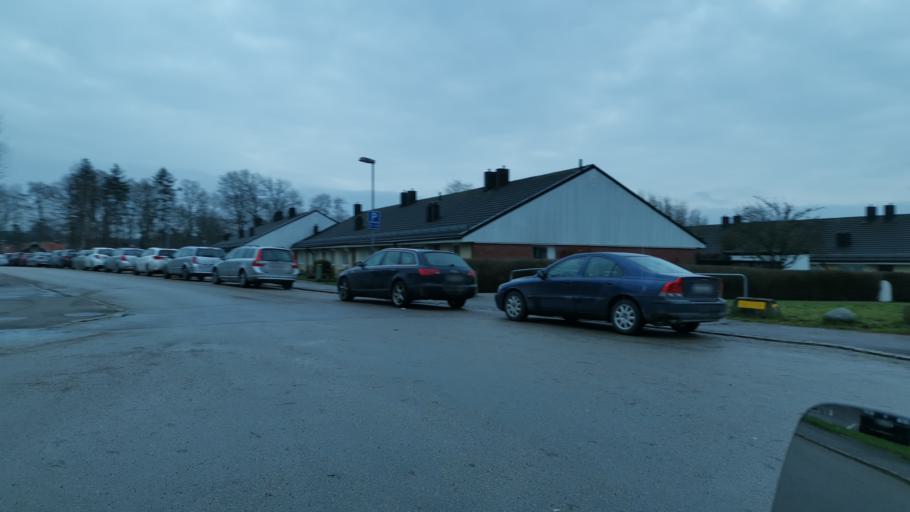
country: SE
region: Vaestra Goetaland
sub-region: Vanersborgs Kommun
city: Vanersborg
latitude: 58.3625
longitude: 12.3461
